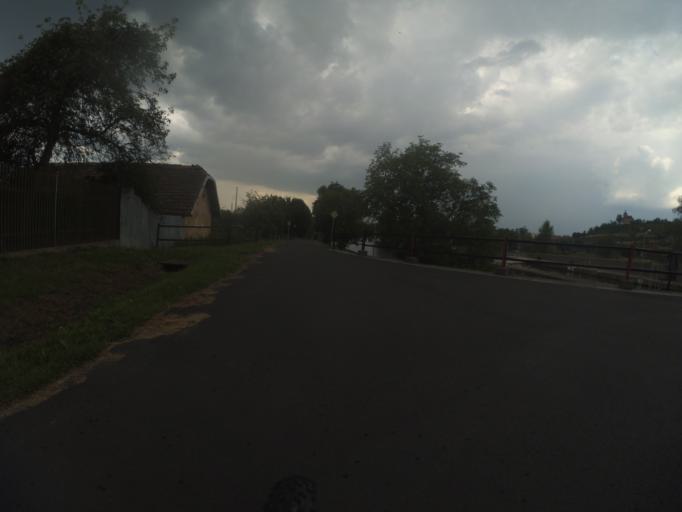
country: CZ
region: Central Bohemia
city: Dolni Berkovice
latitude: 50.4004
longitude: 14.4466
